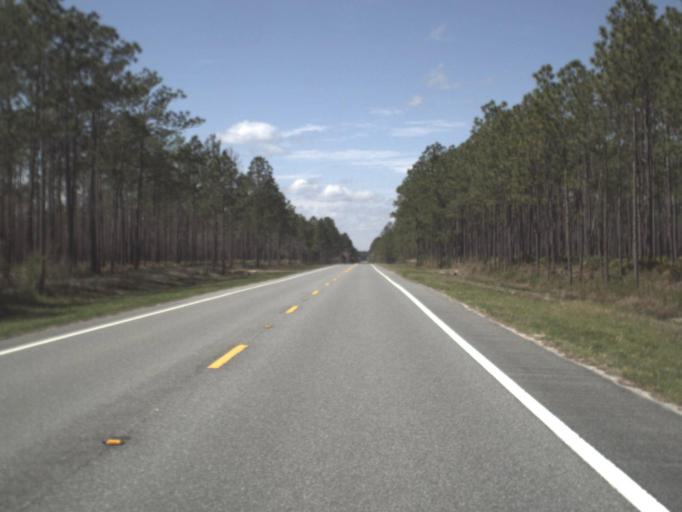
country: US
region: Florida
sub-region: Gadsden County
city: Midway
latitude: 30.3464
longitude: -84.5039
